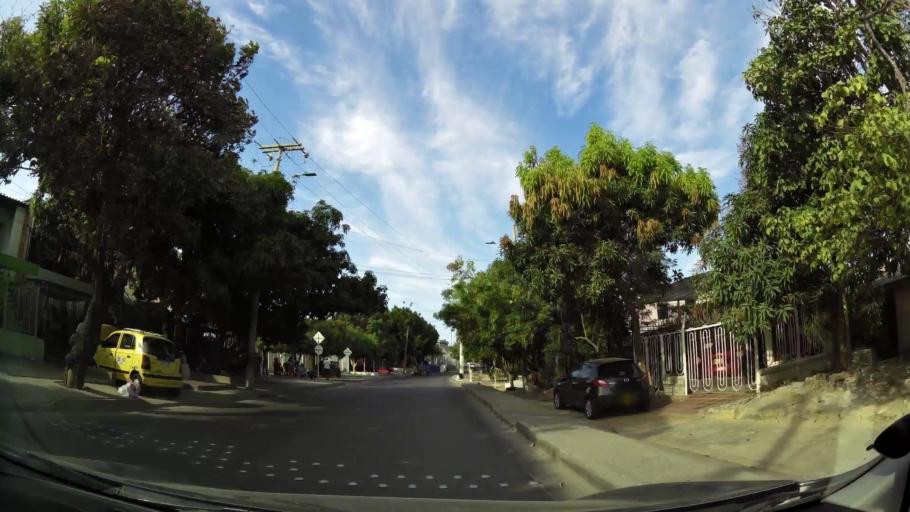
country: CO
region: Atlantico
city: Soledad
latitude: 10.9283
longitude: -74.8108
